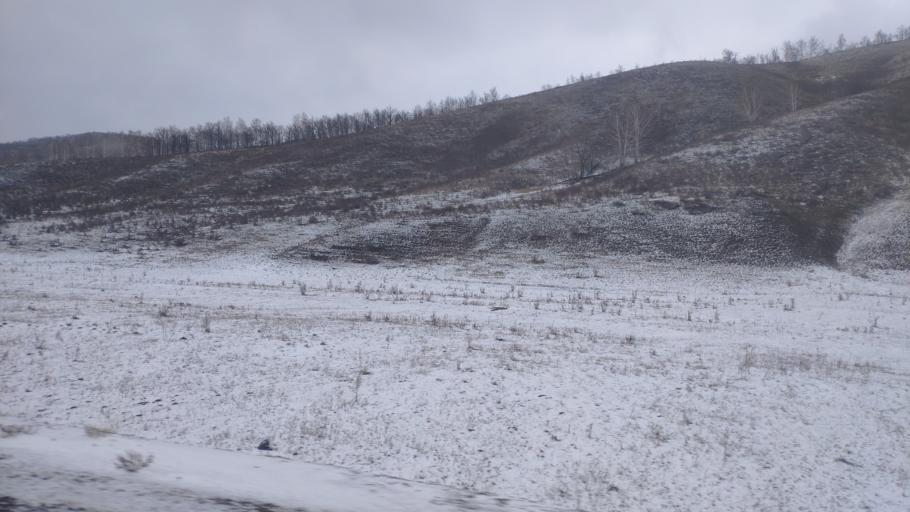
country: RU
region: Bashkortostan
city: Isyangulovo
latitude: 52.1616
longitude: 56.9116
